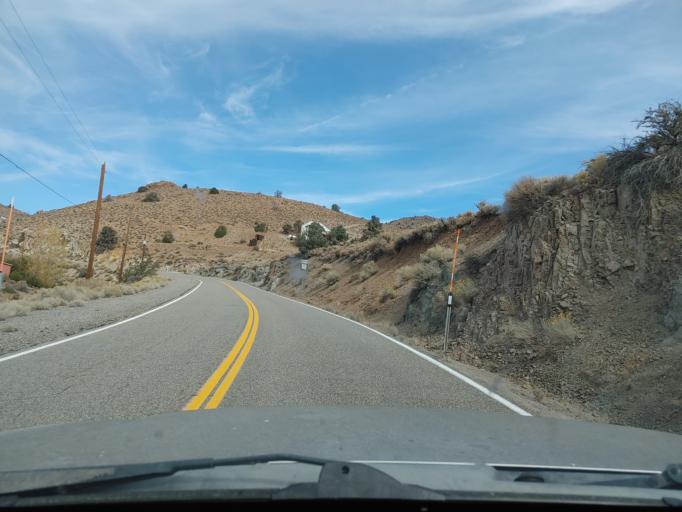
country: US
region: Nevada
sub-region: Lyon County
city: Dayton
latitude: 39.2595
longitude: -119.6338
